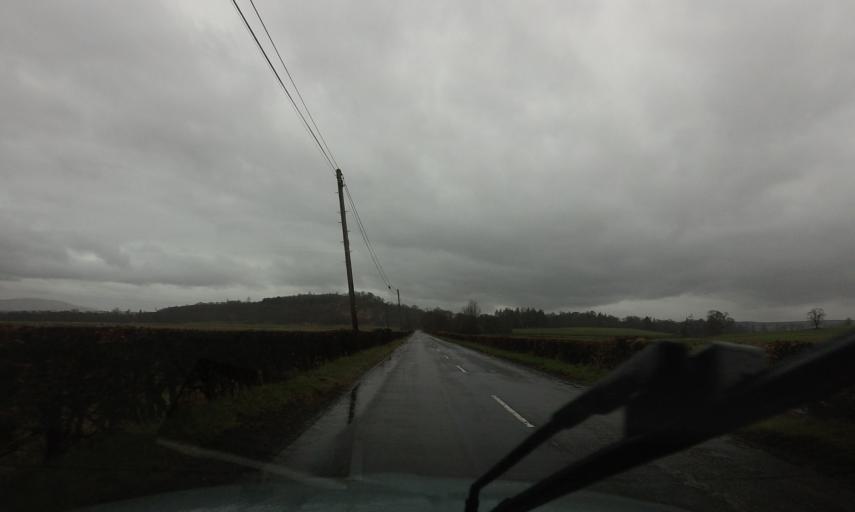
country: GB
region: Scotland
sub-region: Stirling
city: Balfron
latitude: 56.1521
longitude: -4.3616
